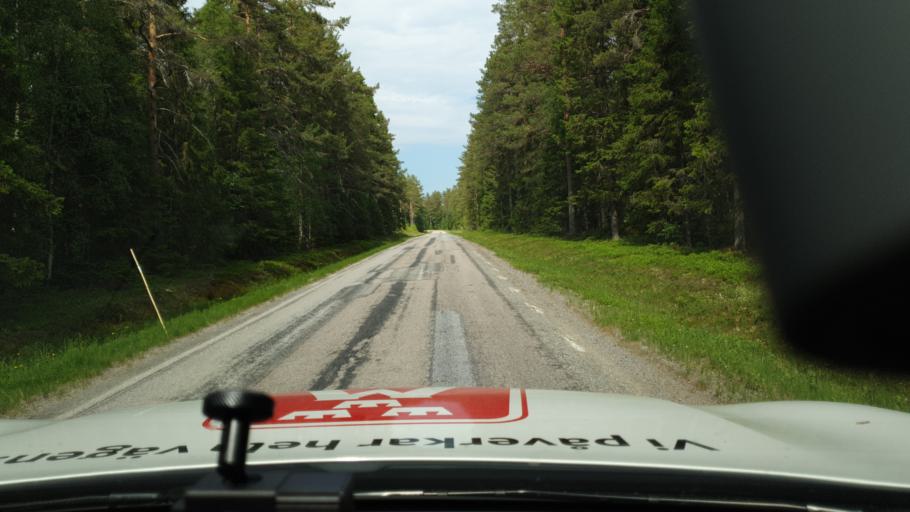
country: SE
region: Vaesterbotten
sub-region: Nordmalings Kommun
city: Nordmaling
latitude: 63.5335
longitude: 19.7134
